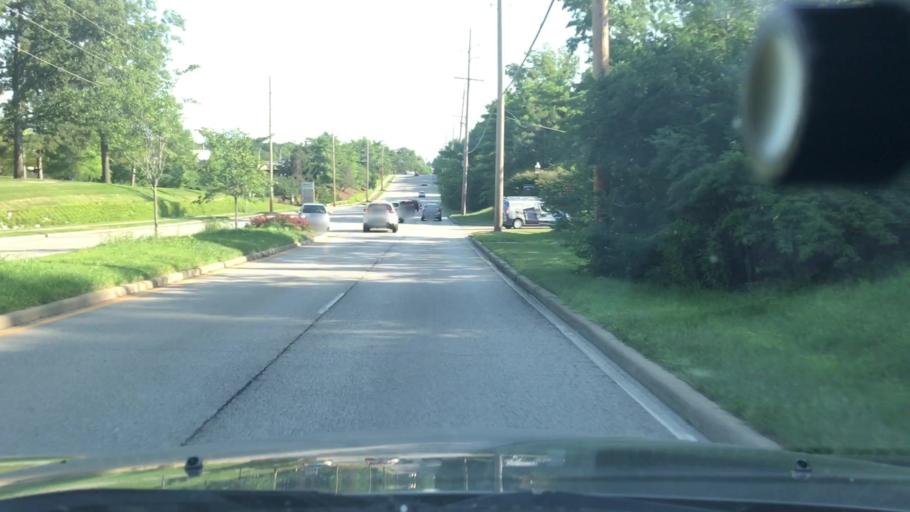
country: US
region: Missouri
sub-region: Saint Louis County
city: Creve Coeur
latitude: 38.6433
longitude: -90.4433
